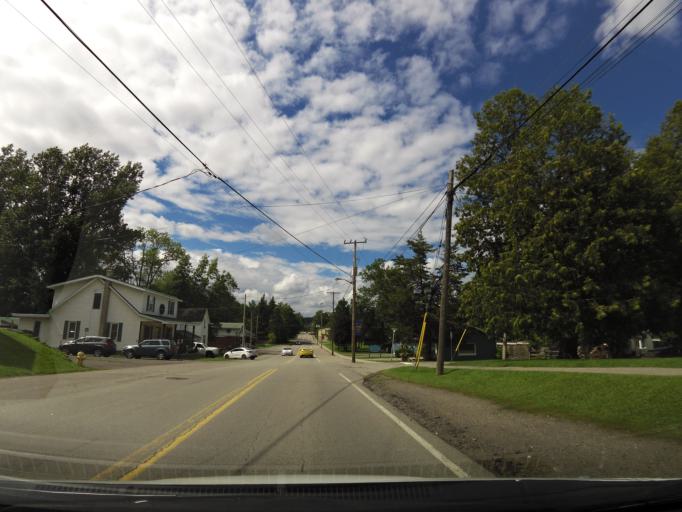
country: CA
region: Ontario
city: Perth
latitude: 44.6758
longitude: -76.3993
